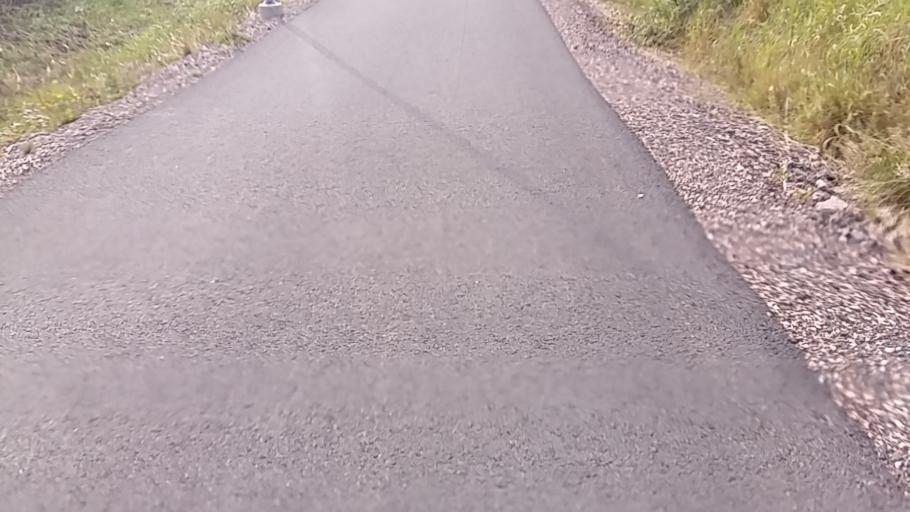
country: SE
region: Joenkoeping
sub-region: Jonkopings Kommun
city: Odensjo
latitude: 57.7259
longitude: 14.1393
